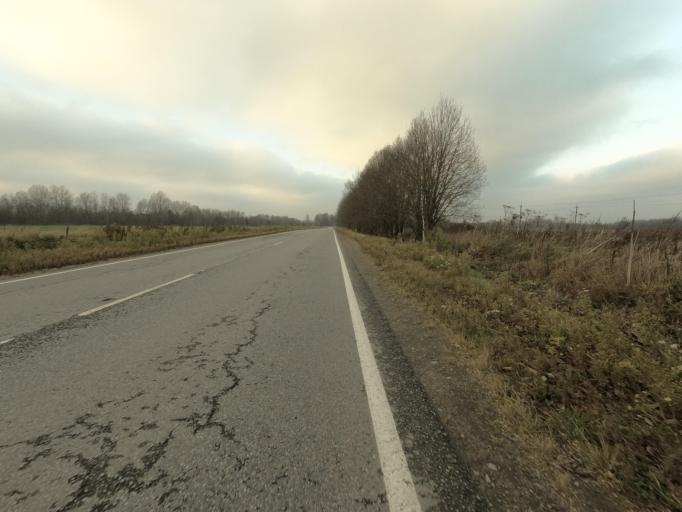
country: RU
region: Leningrad
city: Mga
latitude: 59.7683
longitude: 31.0207
